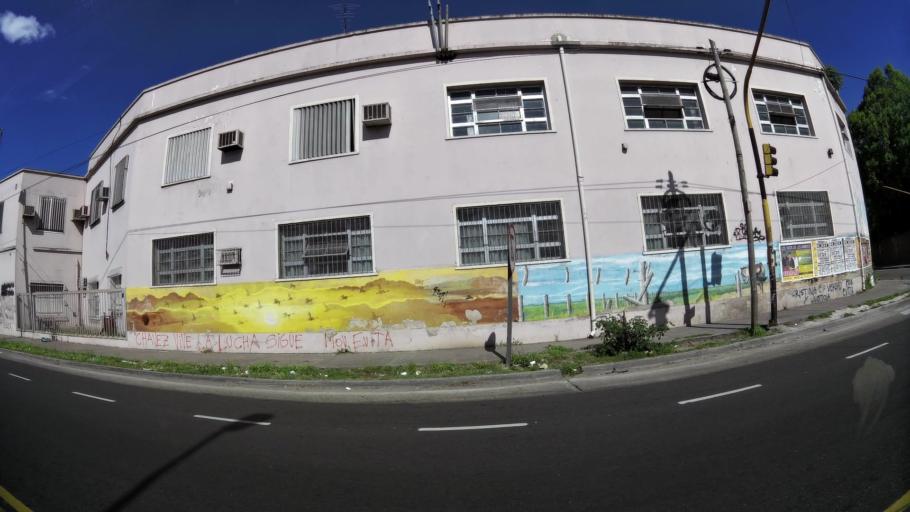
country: AR
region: Buenos Aires
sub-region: Partido de General San Martin
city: General San Martin
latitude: -34.5242
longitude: -58.5716
